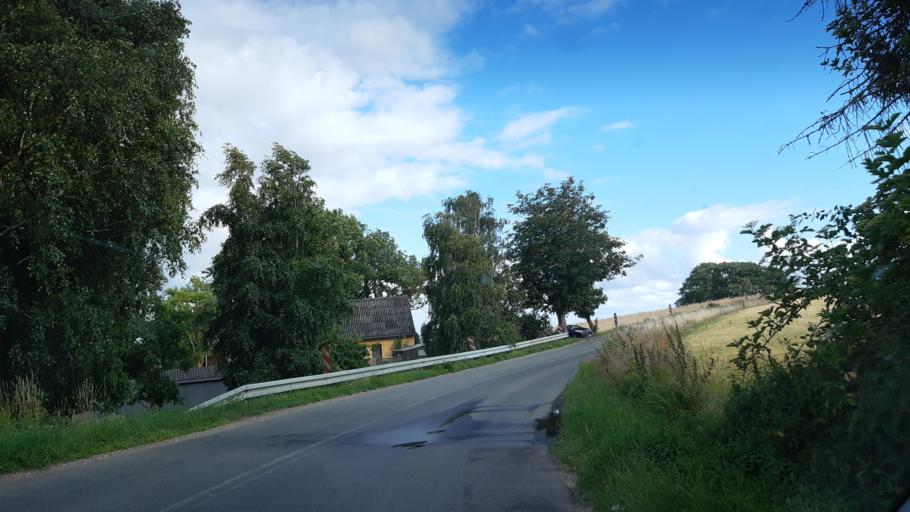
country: DK
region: Zealand
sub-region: Odsherred Kommune
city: Horve
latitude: 55.8123
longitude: 11.4314
